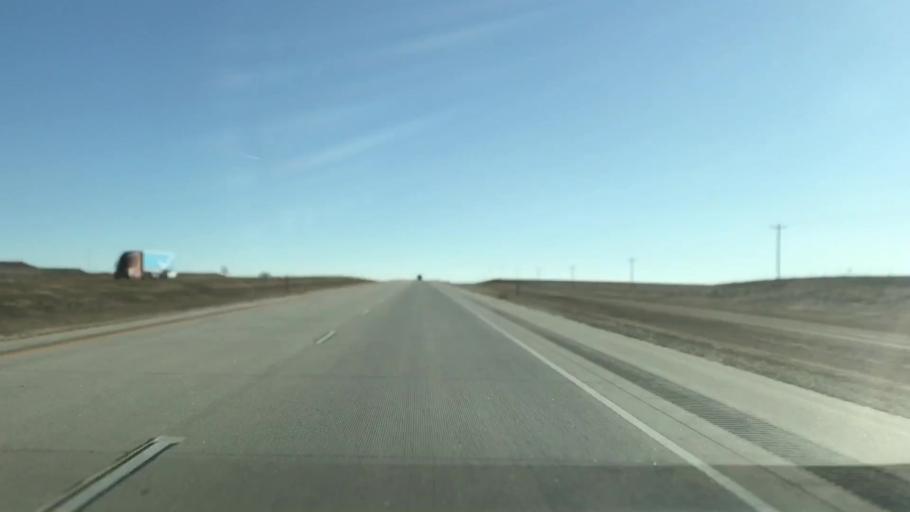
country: US
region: Colorado
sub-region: Lincoln County
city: Limon
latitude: 39.2652
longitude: -103.5721
